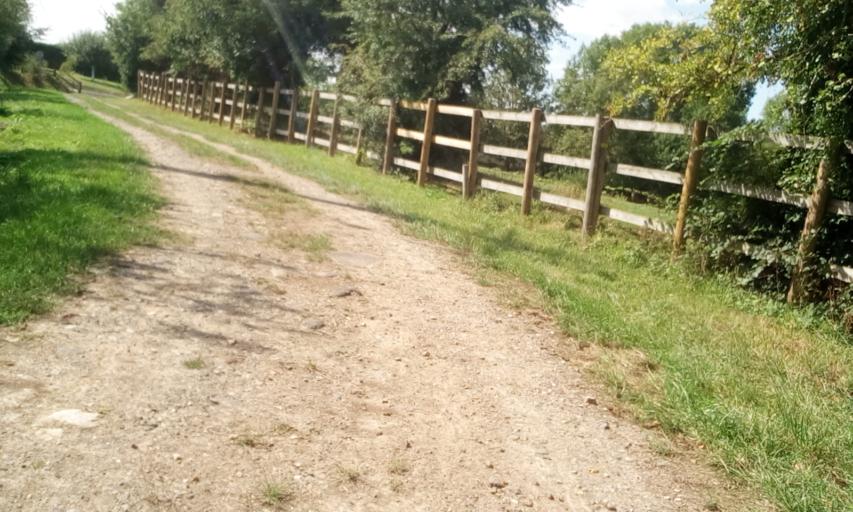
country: FR
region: Lower Normandy
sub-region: Departement du Calvados
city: Argences
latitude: 49.1472
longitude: -0.1113
